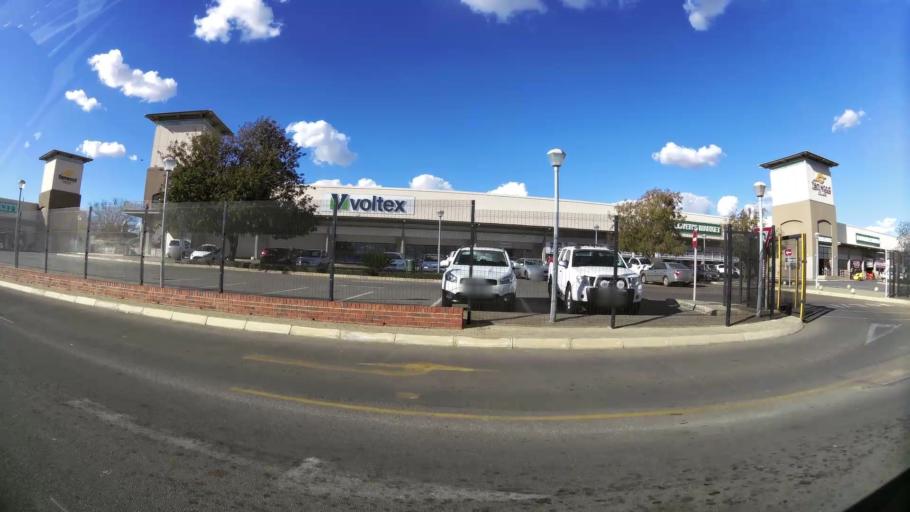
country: ZA
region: North-West
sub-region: Dr Kenneth Kaunda District Municipality
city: Klerksdorp
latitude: -26.8546
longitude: 26.6773
